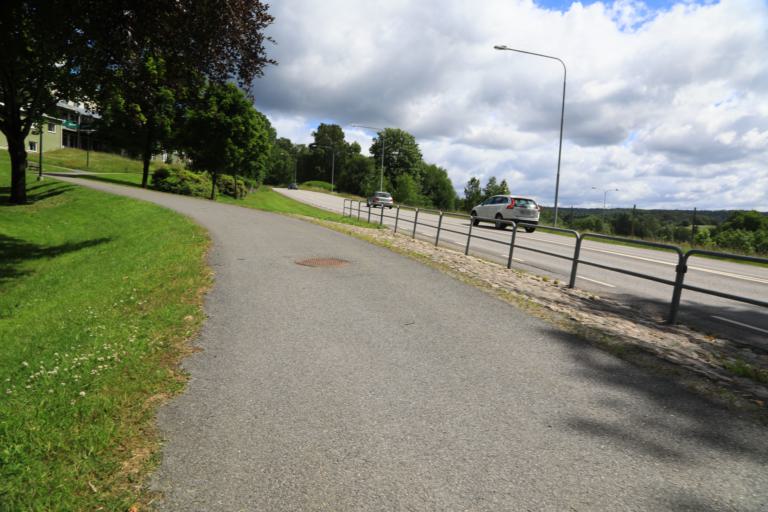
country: SE
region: Vaestra Goetaland
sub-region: Marks Kommun
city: Kinna
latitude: 57.5069
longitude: 12.6985
